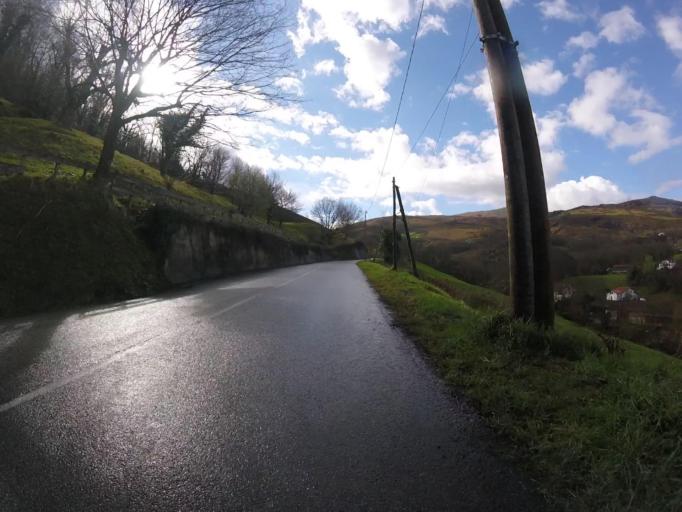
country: FR
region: Aquitaine
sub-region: Departement des Pyrenees-Atlantiques
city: Ascain
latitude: 43.3401
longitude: -1.6157
